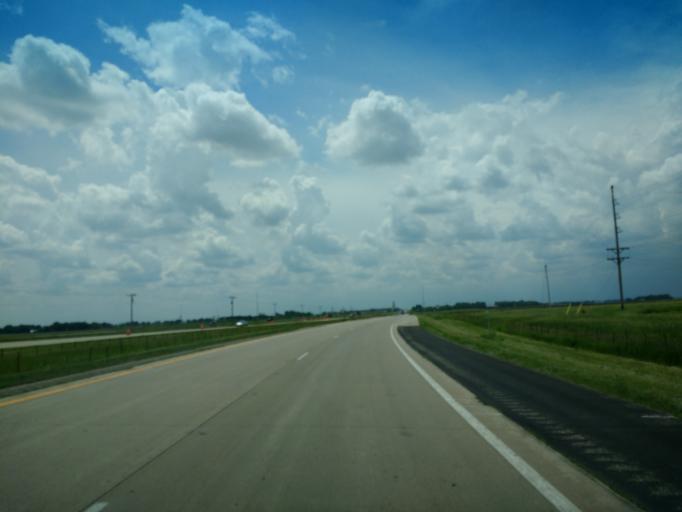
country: US
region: Minnesota
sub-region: Jackson County
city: Lakefield
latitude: 43.7904
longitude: -95.3307
